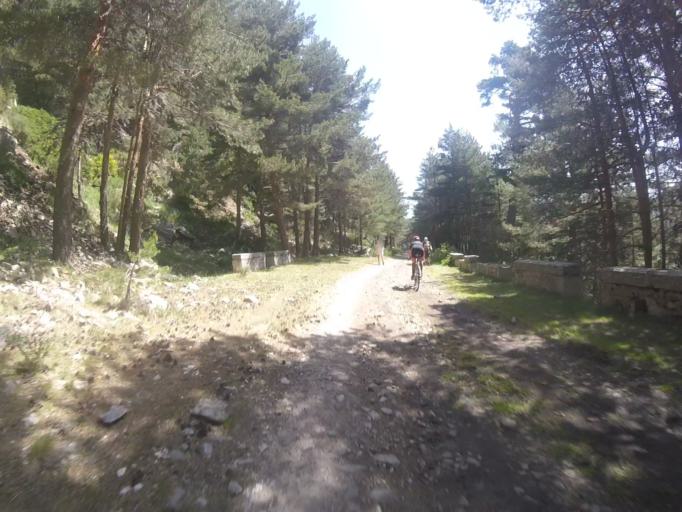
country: ES
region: Madrid
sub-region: Provincia de Madrid
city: Cercedilla
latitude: 40.7987
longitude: -4.0613
